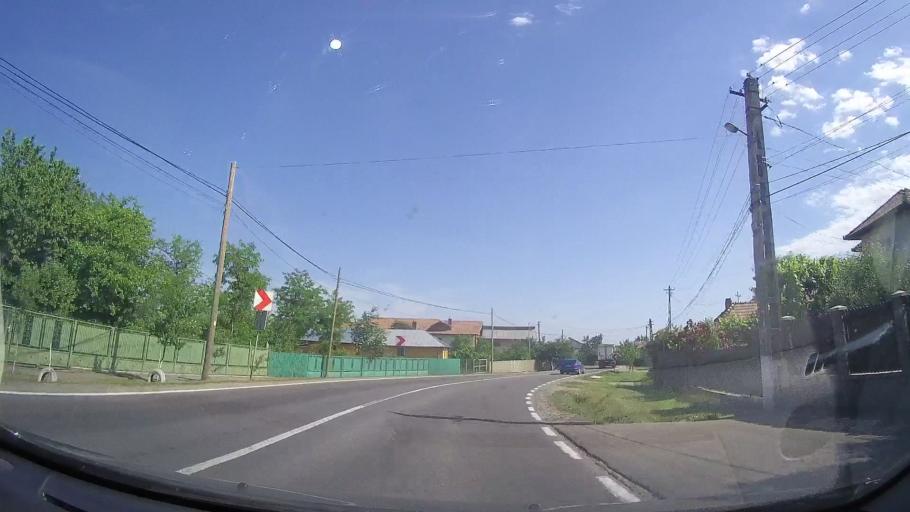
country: RO
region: Prahova
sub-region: Comuna Izvoarele
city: Homoraciu
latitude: 45.2593
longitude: 26.0179
